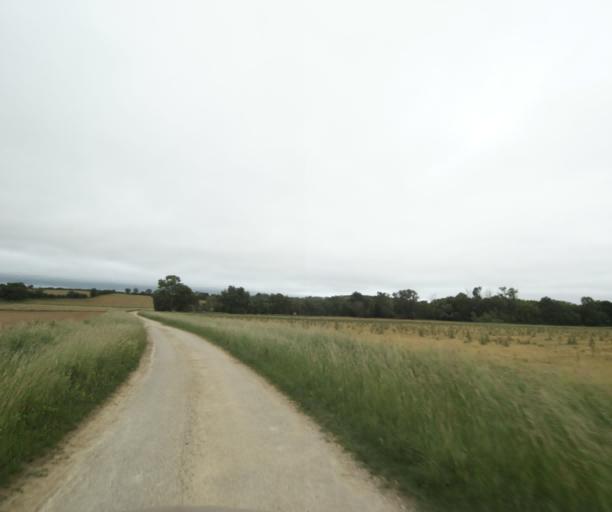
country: FR
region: Rhone-Alpes
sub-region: Departement de l'Ain
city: Tramoyes
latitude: 45.8550
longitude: 4.9448
